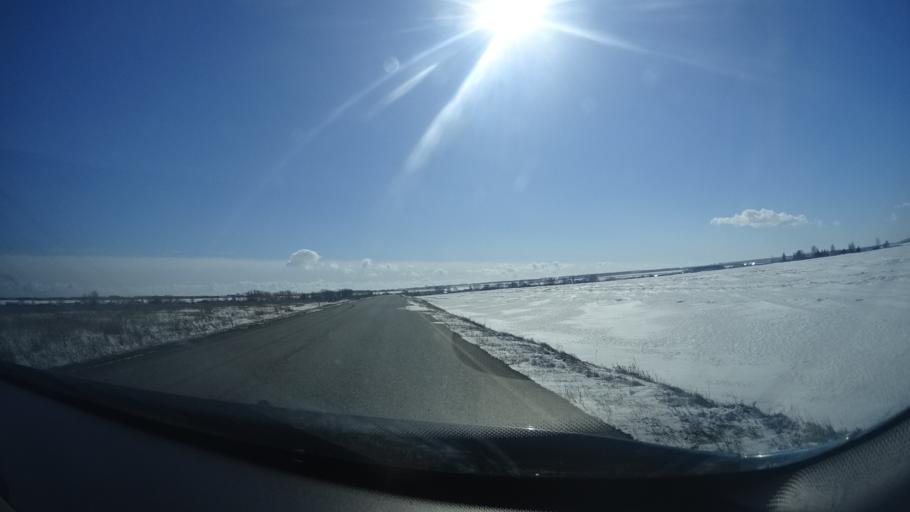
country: RU
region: Bashkortostan
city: Avdon
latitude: 54.5902
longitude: 55.8552
